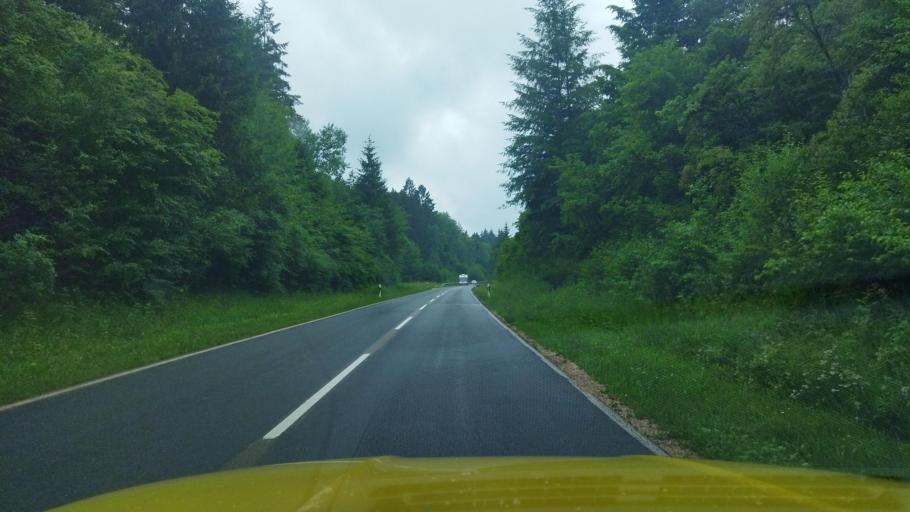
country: DE
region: Bavaria
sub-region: Lower Bavaria
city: Riedenburg
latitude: 48.9437
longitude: 11.6691
